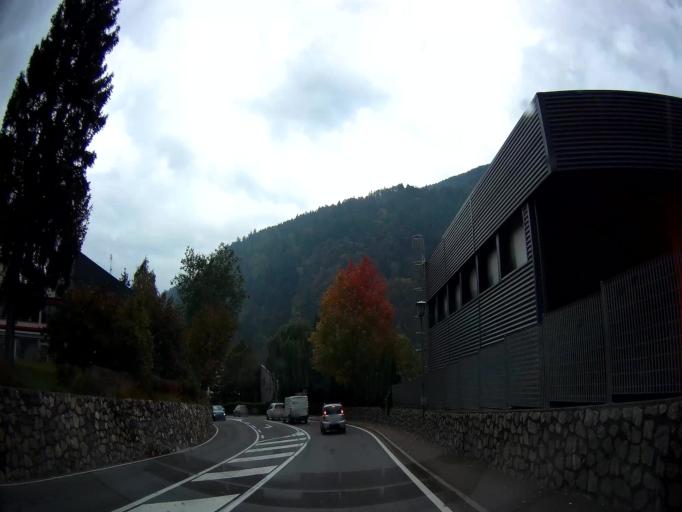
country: IT
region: Trentino-Alto Adige
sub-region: Bolzano
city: Parcines
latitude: 46.6739
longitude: 11.0790
